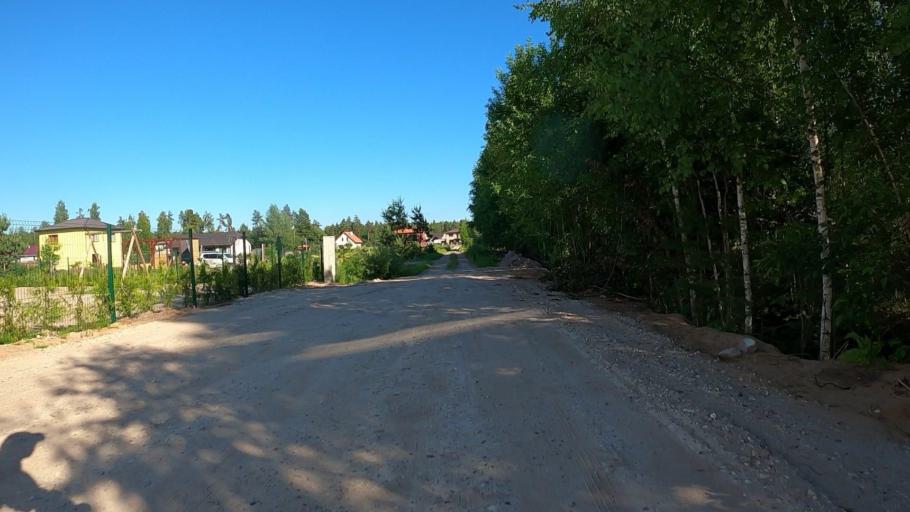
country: LV
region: Stopini
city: Ulbroka
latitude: 56.8802
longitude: 24.2908
